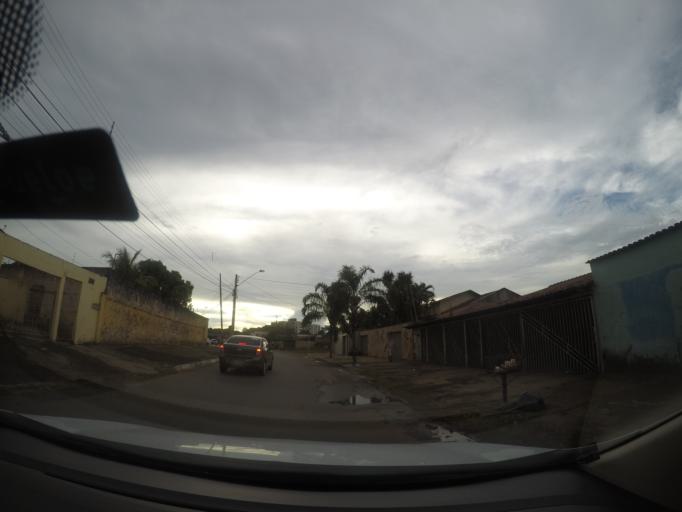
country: BR
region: Goias
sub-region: Goiania
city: Goiania
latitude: -16.6889
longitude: -49.3039
